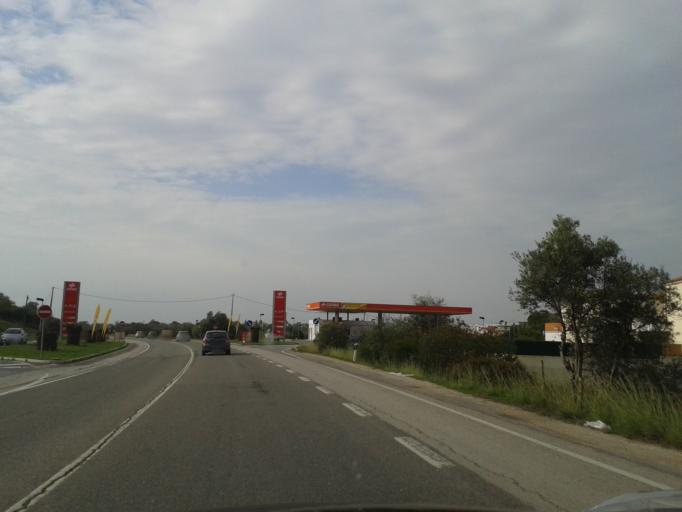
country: PT
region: Faro
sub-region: Albufeira
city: Ferreiras
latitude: 37.1233
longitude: -8.2308
